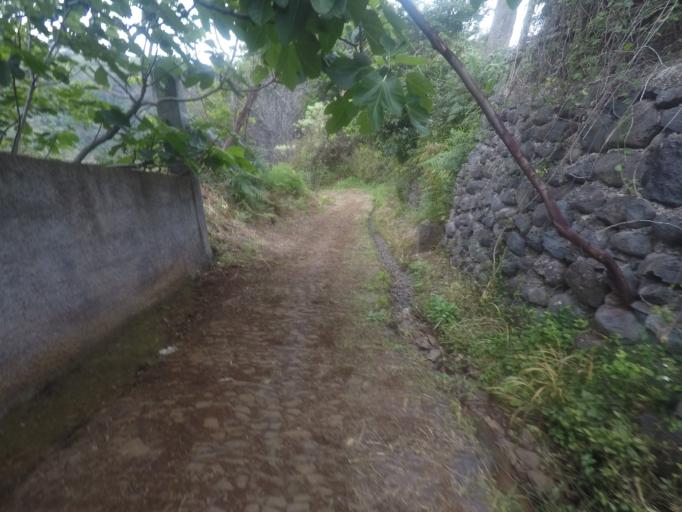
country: PT
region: Madeira
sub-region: Santana
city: Santana
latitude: 32.8271
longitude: -16.8938
